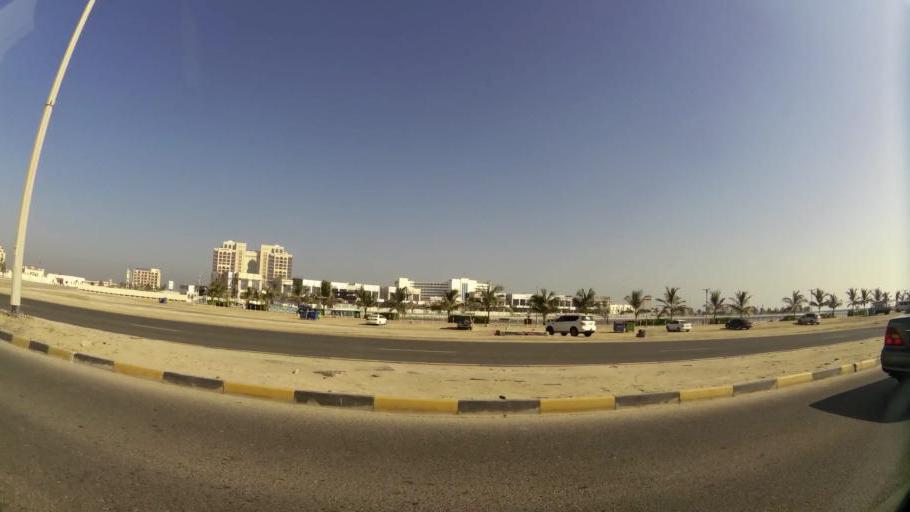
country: AE
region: Ajman
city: Ajman
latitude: 25.4184
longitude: 55.4456
